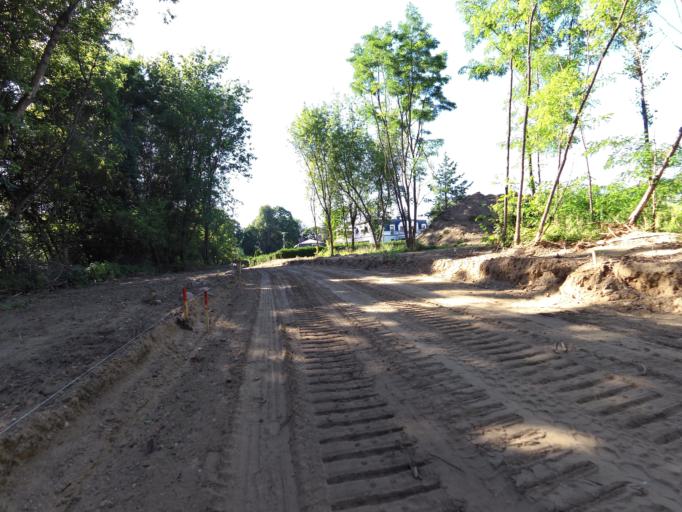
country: LT
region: Vilnius County
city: Vilkpede
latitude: 54.6853
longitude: 25.2529
